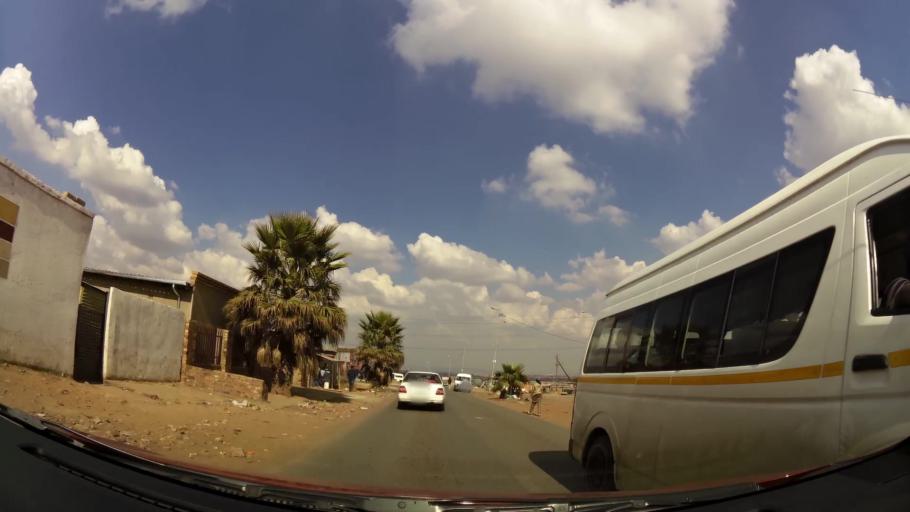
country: ZA
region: Gauteng
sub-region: City of Johannesburg Metropolitan Municipality
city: Roodepoort
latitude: -26.1943
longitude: 27.8683
